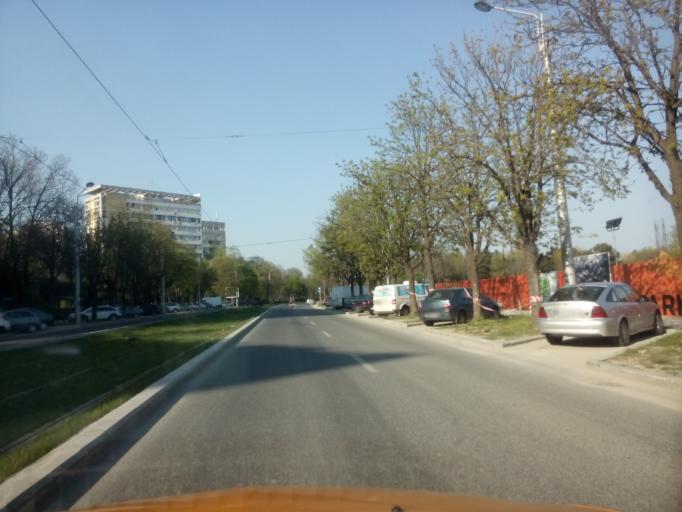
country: RO
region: Ilfov
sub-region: Comuna Fundeni-Dobroesti
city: Fundeni
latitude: 44.4216
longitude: 26.1492
